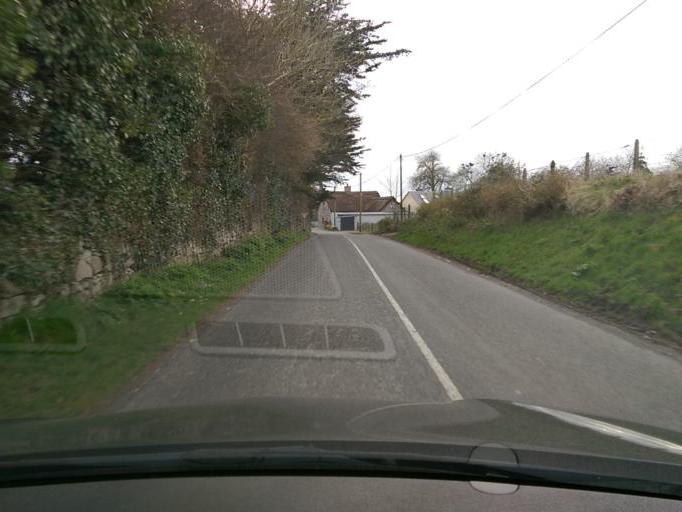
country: IE
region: Leinster
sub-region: Uibh Fhaili
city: Banagher
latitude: 53.2797
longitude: -8.0377
